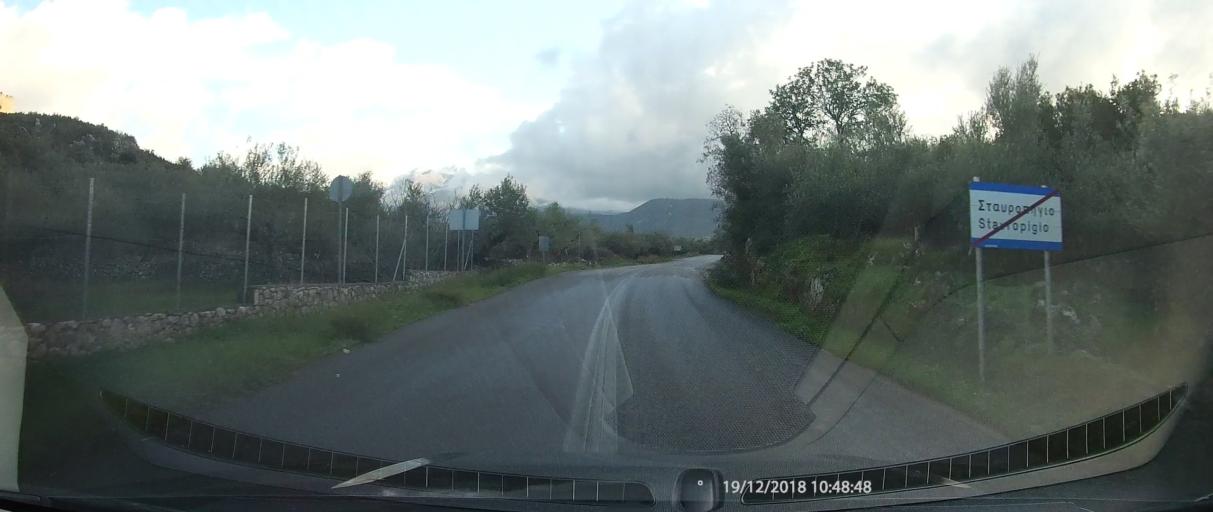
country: GR
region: Peloponnese
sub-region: Nomos Messinias
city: Kardamyli
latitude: 36.9283
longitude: 22.1912
